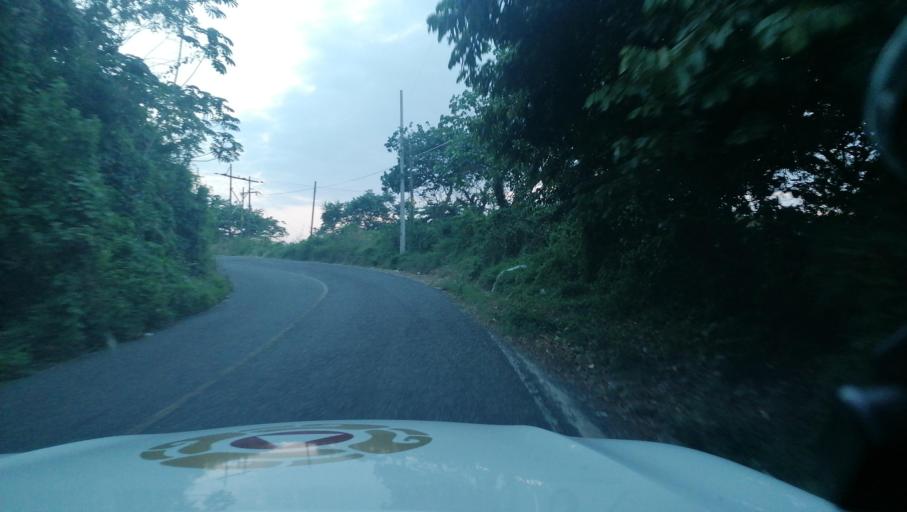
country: MX
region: Chiapas
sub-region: Cacahoatan
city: Benito Juarez
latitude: 15.0409
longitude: -92.2438
